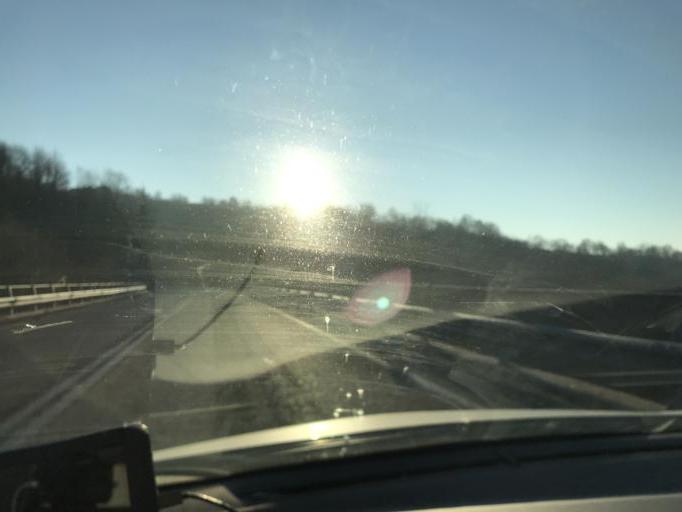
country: IT
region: Latium
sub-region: Provincia di Rieti
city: Petrella Salto
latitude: 42.3055
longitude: 13.0397
